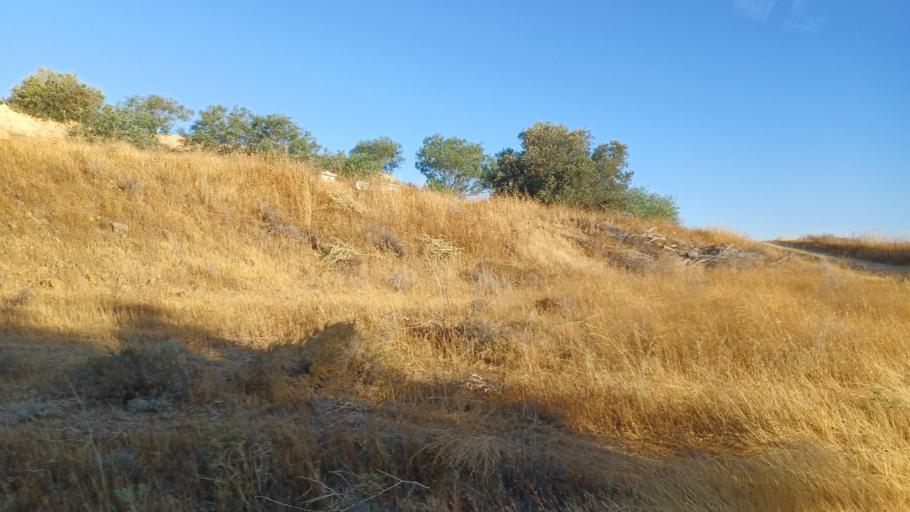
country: CY
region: Larnaka
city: Troulloi
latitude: 35.0281
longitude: 33.6505
